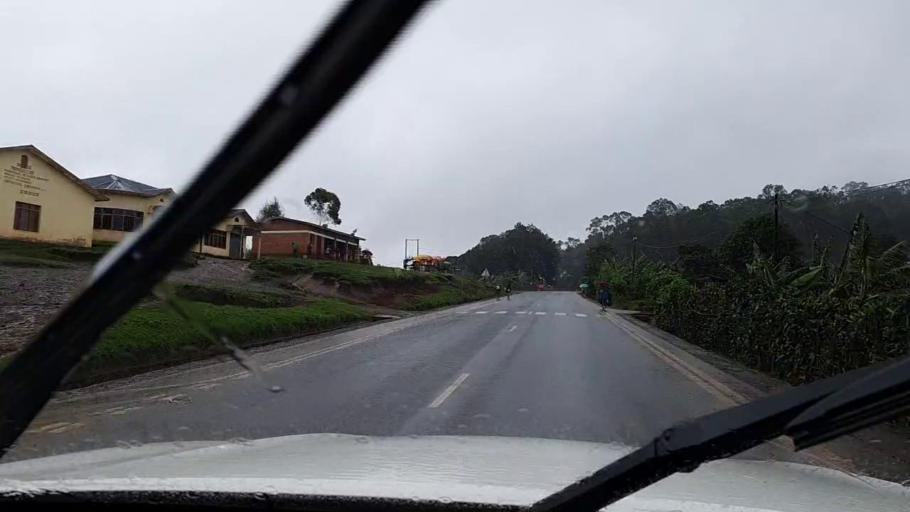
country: RW
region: Western Province
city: Cyangugu
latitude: -2.4625
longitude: 28.9969
